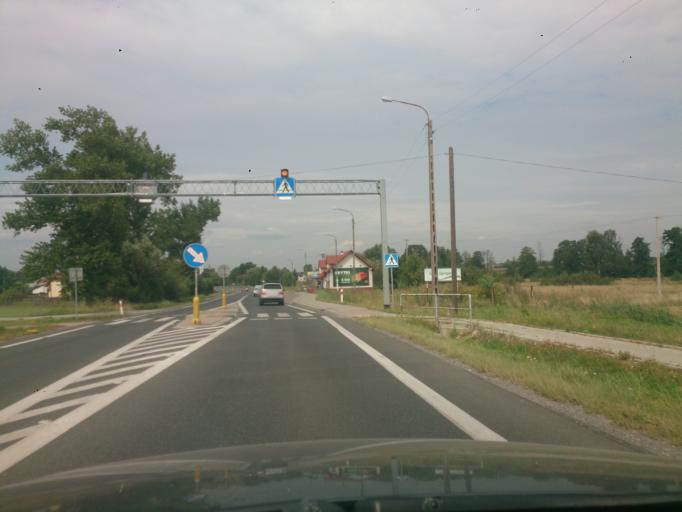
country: PL
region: Subcarpathian Voivodeship
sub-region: Powiat kolbuszowski
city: Kolbuszowa
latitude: 50.2148
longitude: 21.8143
